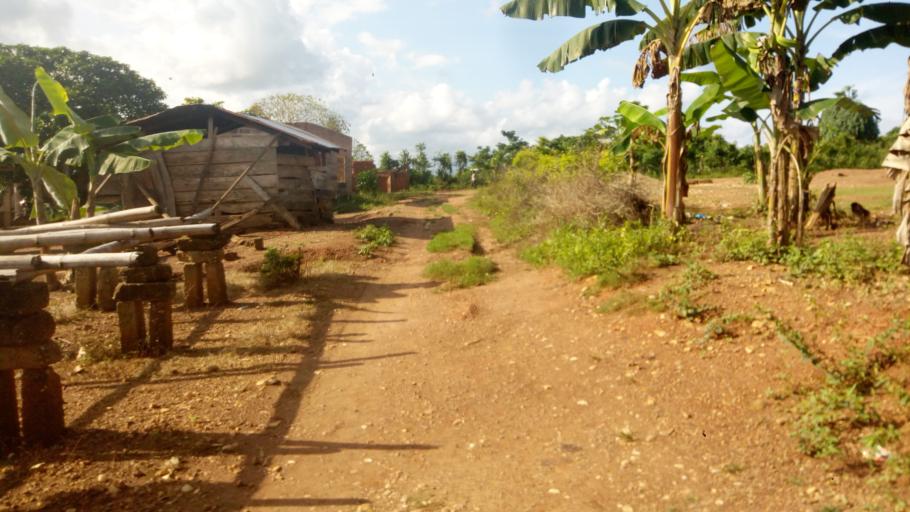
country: GH
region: Eastern
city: Akwatia
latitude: 6.1584
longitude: -0.8142
